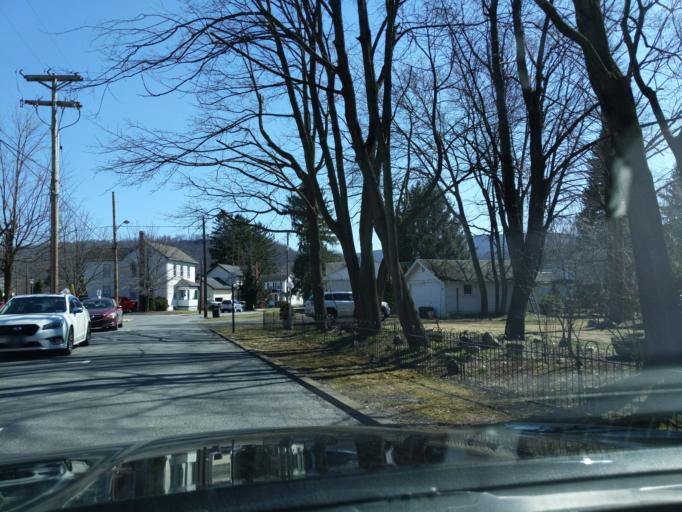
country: US
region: Pennsylvania
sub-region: Blair County
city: Hollidaysburg
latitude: 40.4250
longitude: -78.3989
